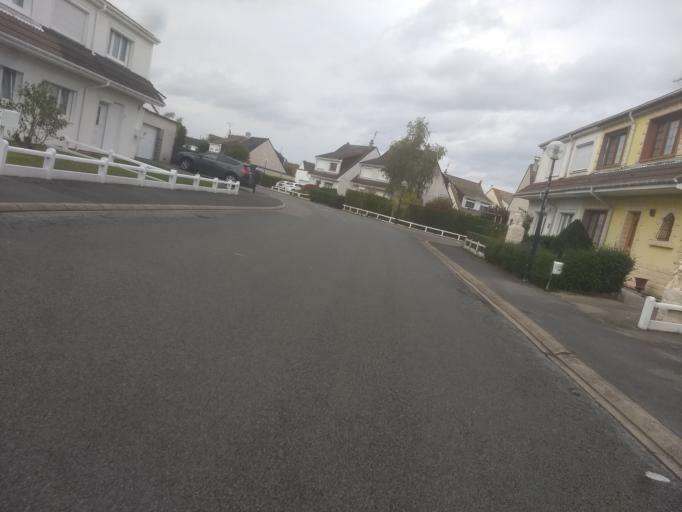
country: FR
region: Nord-Pas-de-Calais
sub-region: Departement du Pas-de-Calais
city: Agny
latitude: 50.2670
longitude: 2.7729
